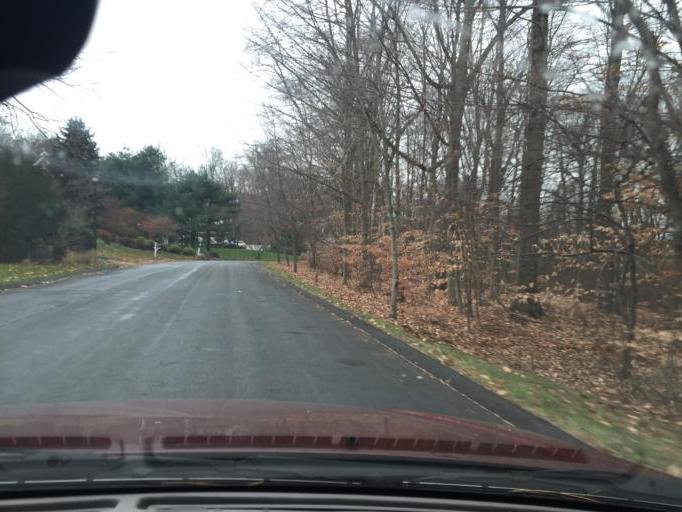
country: US
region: Connecticut
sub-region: Fairfield County
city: Southport
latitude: 41.1456
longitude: -73.2921
